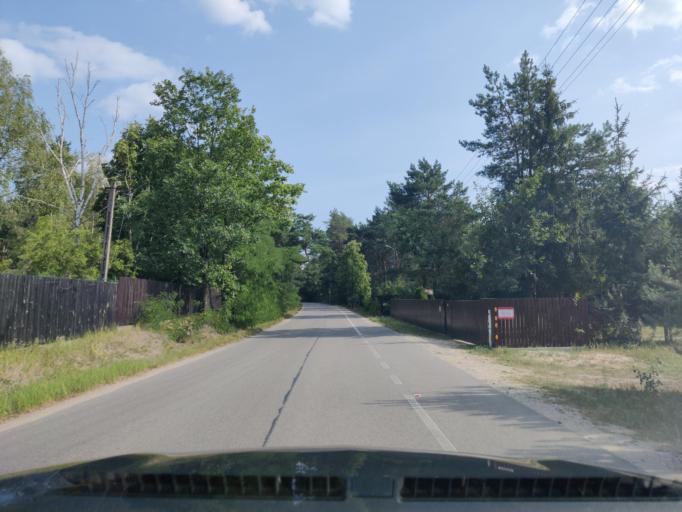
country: PL
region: Masovian Voivodeship
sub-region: Powiat makowski
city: Rozan
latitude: 52.8722
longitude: 21.4326
